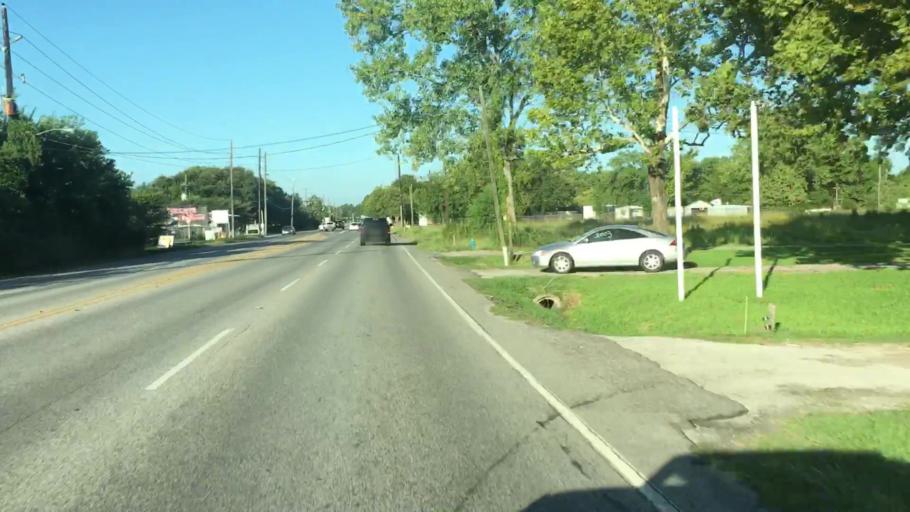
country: US
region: Texas
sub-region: Harris County
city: Humble
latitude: 29.9600
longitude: -95.2578
